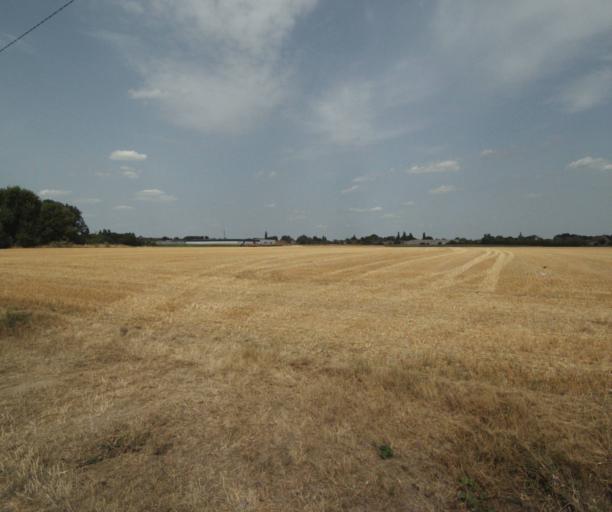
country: BE
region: Wallonia
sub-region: Province du Hainaut
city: Estaimpuis
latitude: 50.7008
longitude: 3.2533
